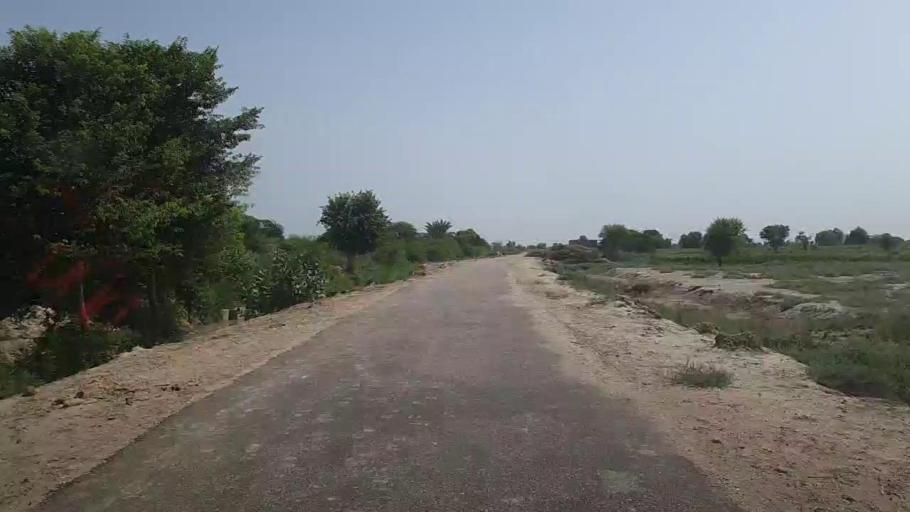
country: PK
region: Sindh
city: Pad Idan
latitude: 26.8298
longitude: 68.3304
